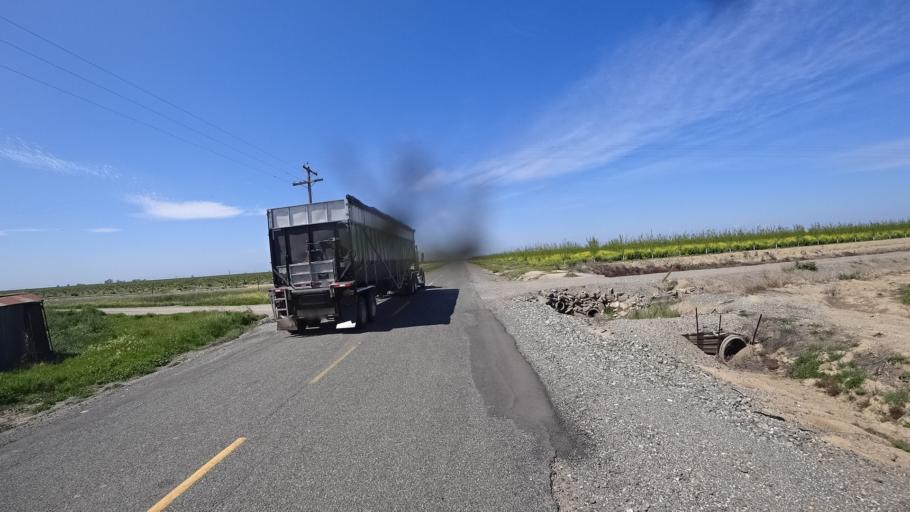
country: US
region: California
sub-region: Glenn County
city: Orland
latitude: 39.6528
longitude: -122.1315
